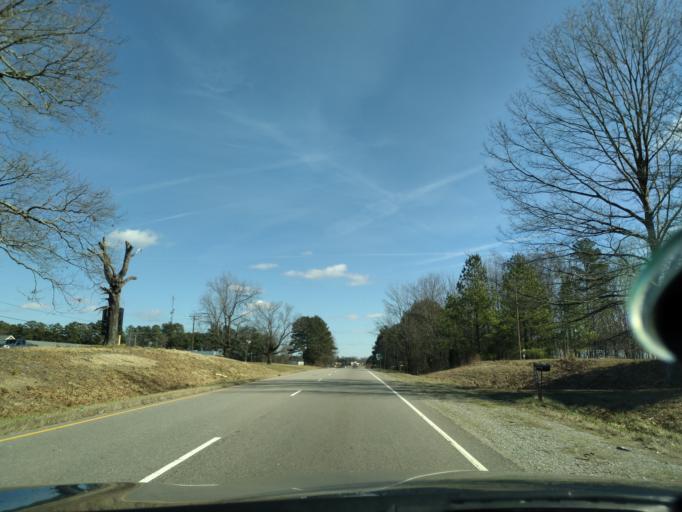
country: US
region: Virginia
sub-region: Nottoway County
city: Crewe
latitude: 37.1901
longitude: -78.1613
